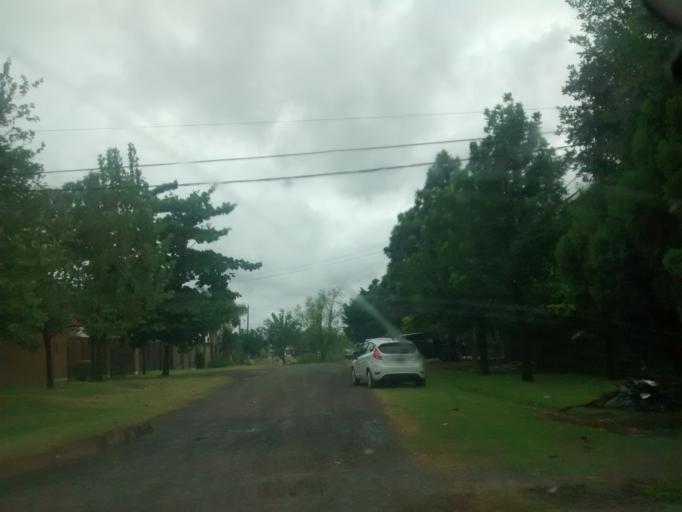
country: AR
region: Chaco
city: Resistencia
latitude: -27.4391
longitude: -58.9679
